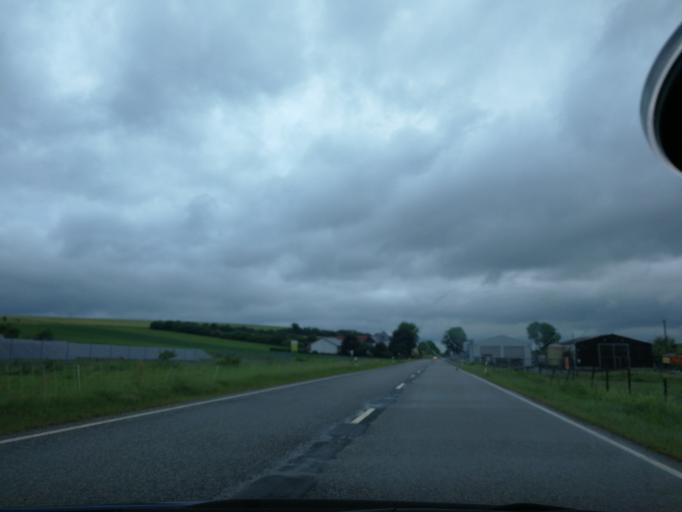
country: DE
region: Rheinland-Pfalz
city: Borrstadt
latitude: 49.5856
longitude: 7.9478
